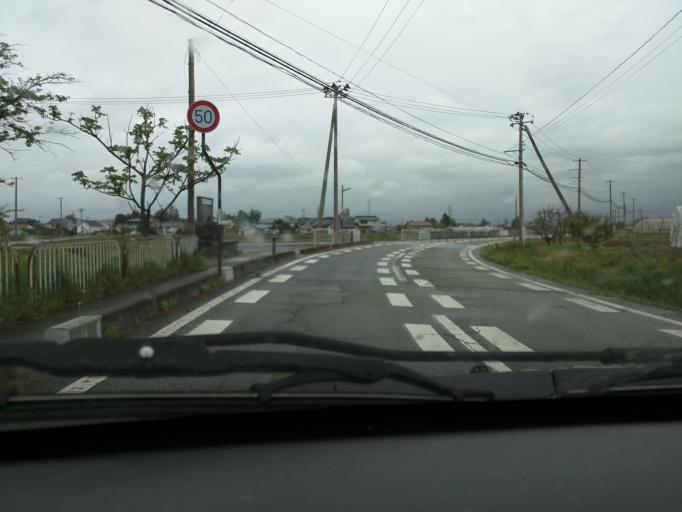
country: JP
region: Fukushima
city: Kitakata
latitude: 37.5698
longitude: 139.8739
